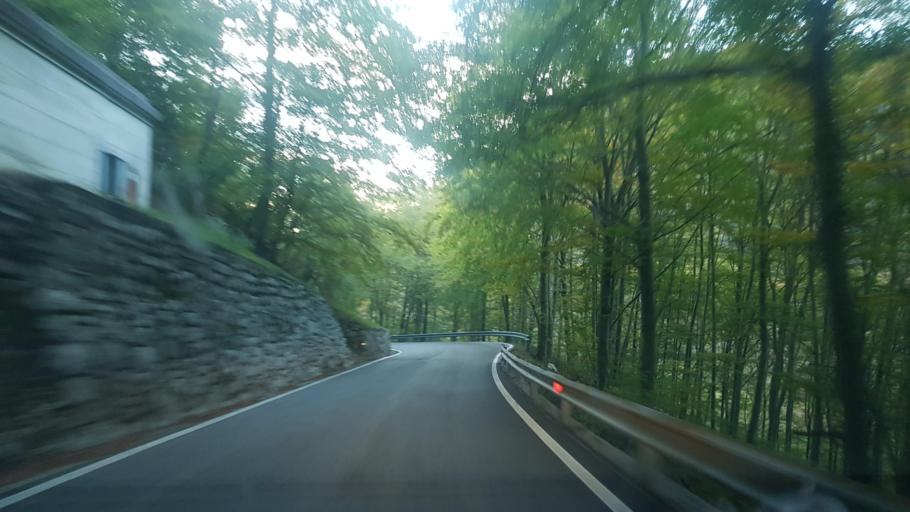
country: IT
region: Friuli Venezia Giulia
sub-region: Provincia di Udine
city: Villa Santina
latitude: 46.3500
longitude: 12.9157
